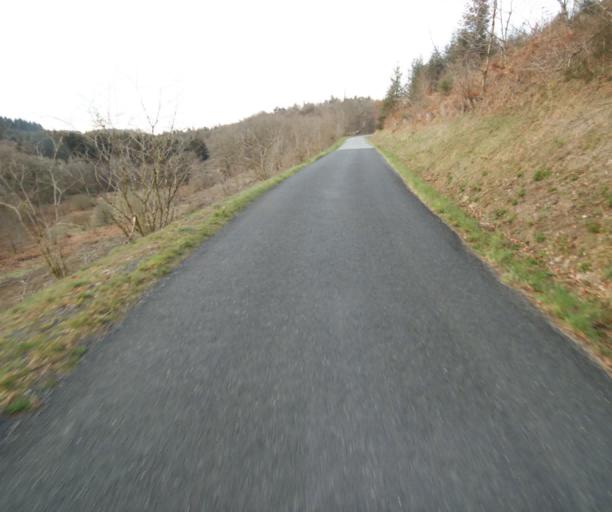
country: FR
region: Limousin
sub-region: Departement de la Correze
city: Correze
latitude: 45.3827
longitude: 1.8889
